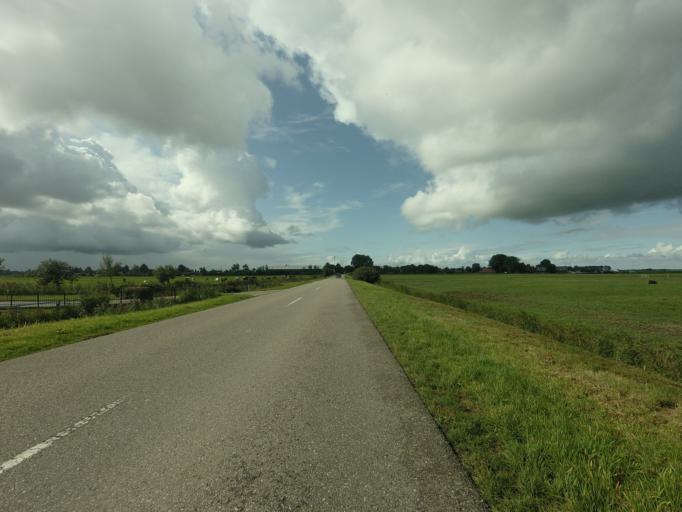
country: NL
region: Friesland
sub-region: Gemeente Boarnsterhim
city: Warten
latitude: 53.1536
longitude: 5.9094
